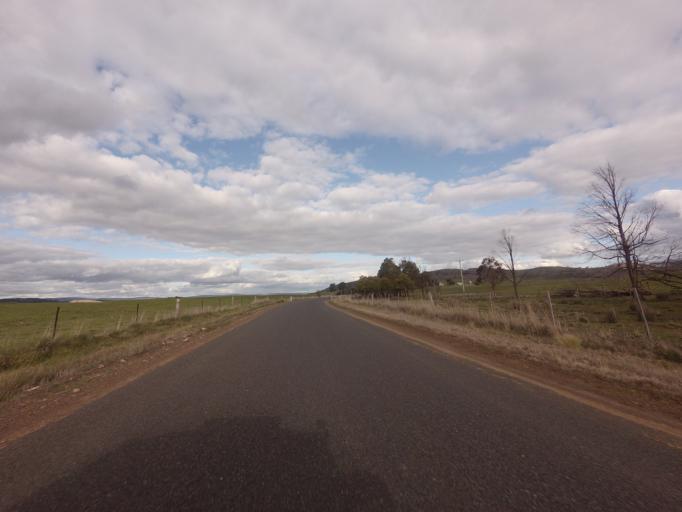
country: AU
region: Tasmania
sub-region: Northern Midlands
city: Evandale
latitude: -41.9009
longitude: 147.3502
